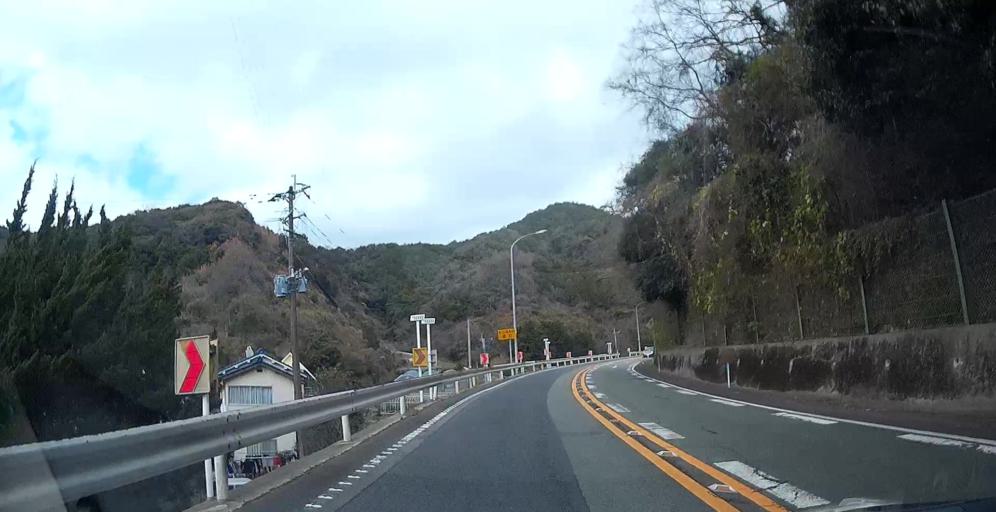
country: JP
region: Kumamoto
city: Minamata
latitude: 32.3344
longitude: 130.4854
